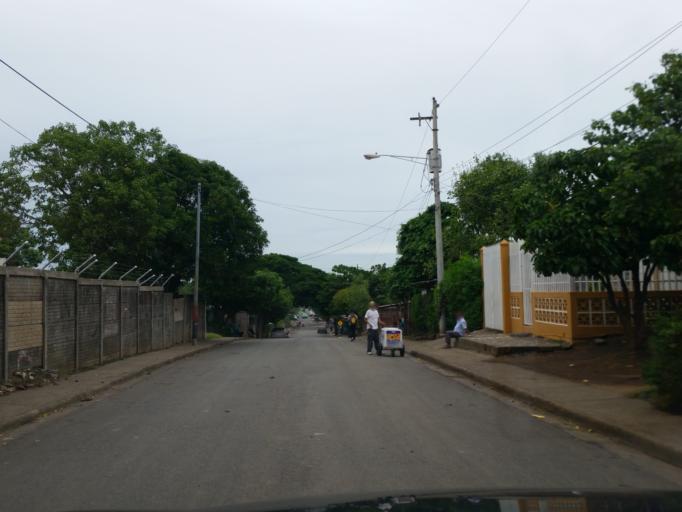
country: NI
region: Managua
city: Managua
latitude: 12.1307
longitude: -86.2780
